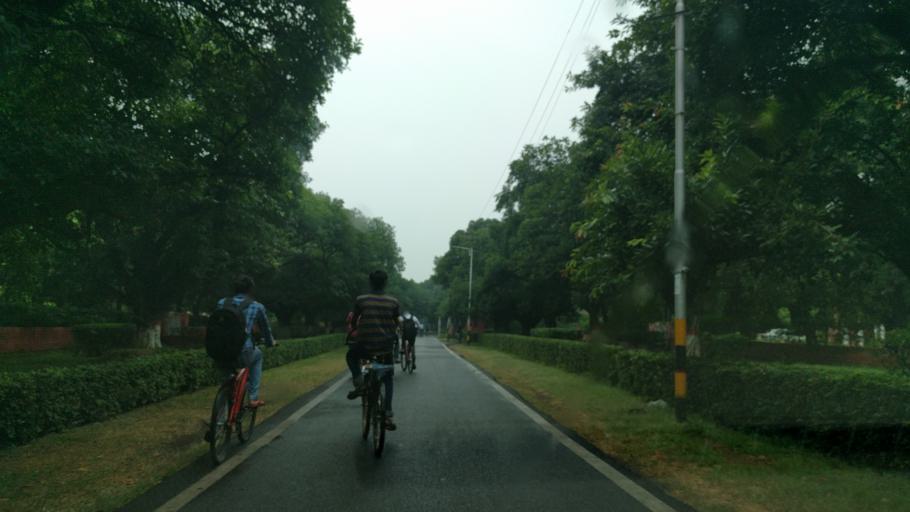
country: IN
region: NCT
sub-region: Central Delhi
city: Karol Bagh
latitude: 28.6382
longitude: 77.1654
